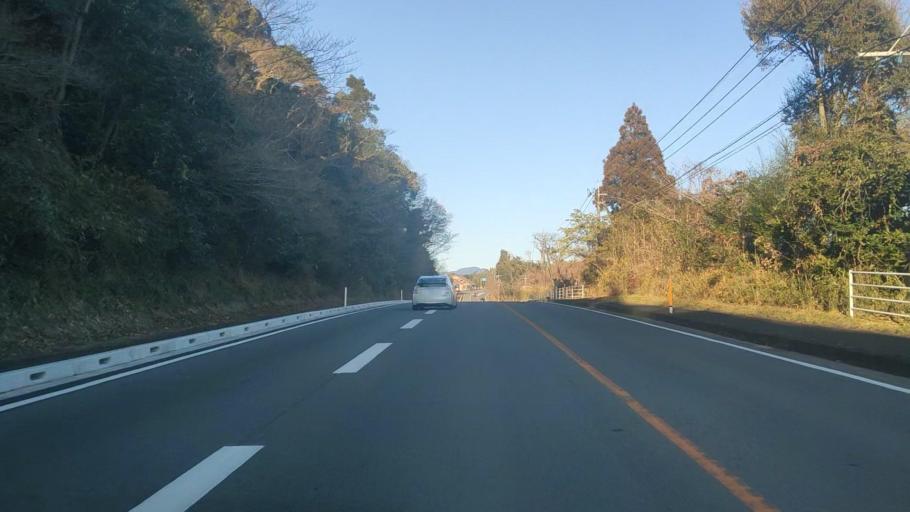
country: JP
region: Miyazaki
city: Takanabe
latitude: 32.1526
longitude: 131.5216
